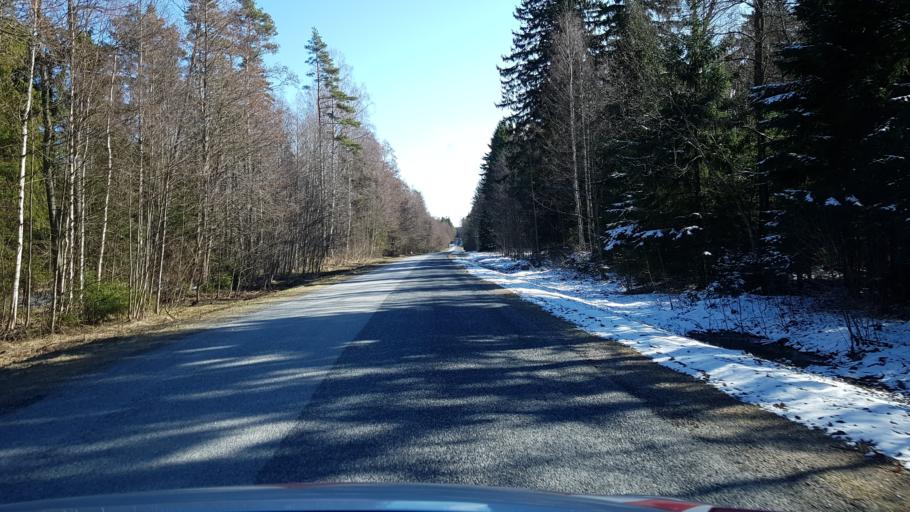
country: EE
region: Harju
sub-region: Loksa linn
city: Loksa
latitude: 59.5625
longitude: 25.8525
